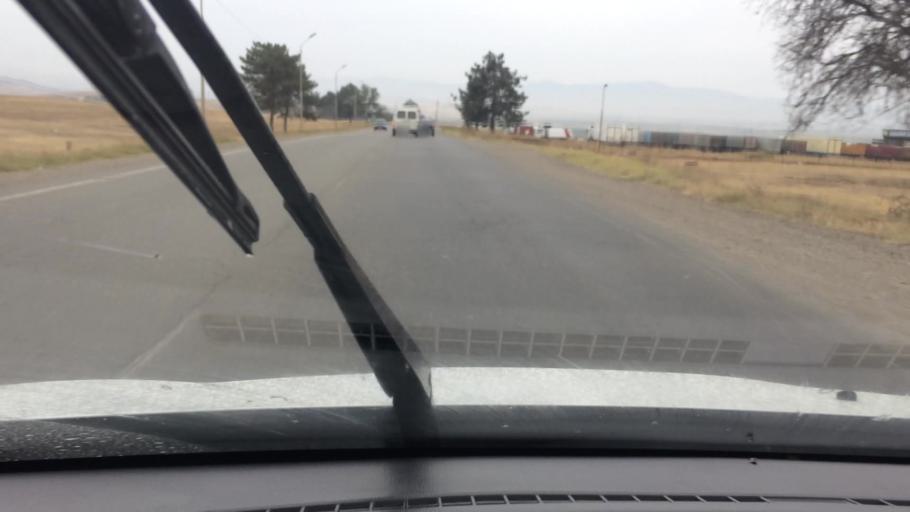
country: GE
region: Kvemo Kartli
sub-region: Marneuli
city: Marneuli
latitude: 41.5116
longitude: 44.7909
